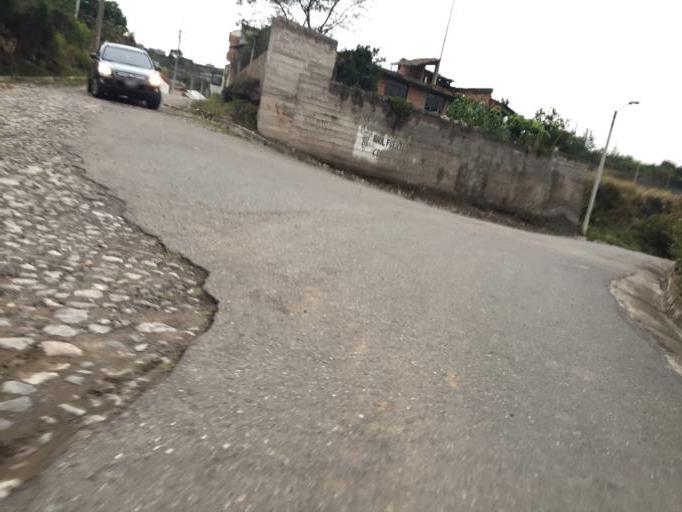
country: EC
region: Imbabura
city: Atuntaqui
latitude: 0.3398
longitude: -78.1723
